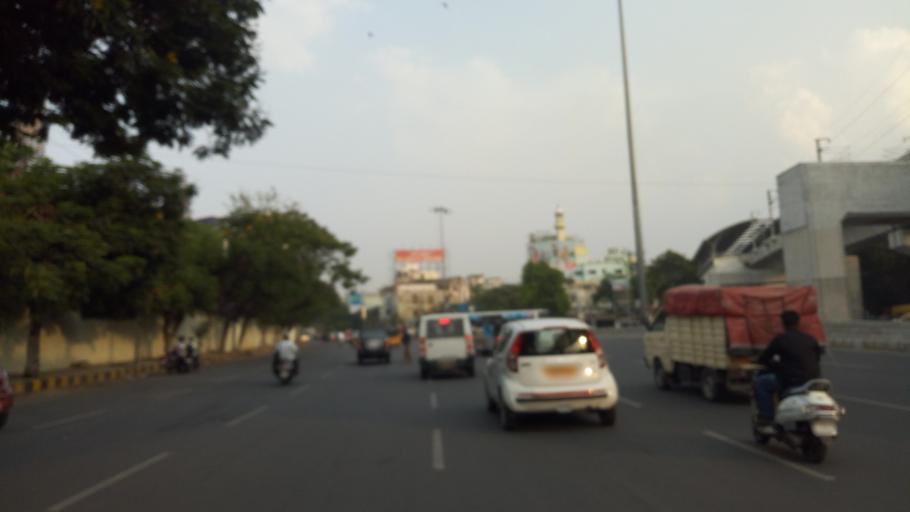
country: IN
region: Telangana
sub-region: Hyderabad
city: Hyderabad
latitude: 17.3999
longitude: 78.4707
